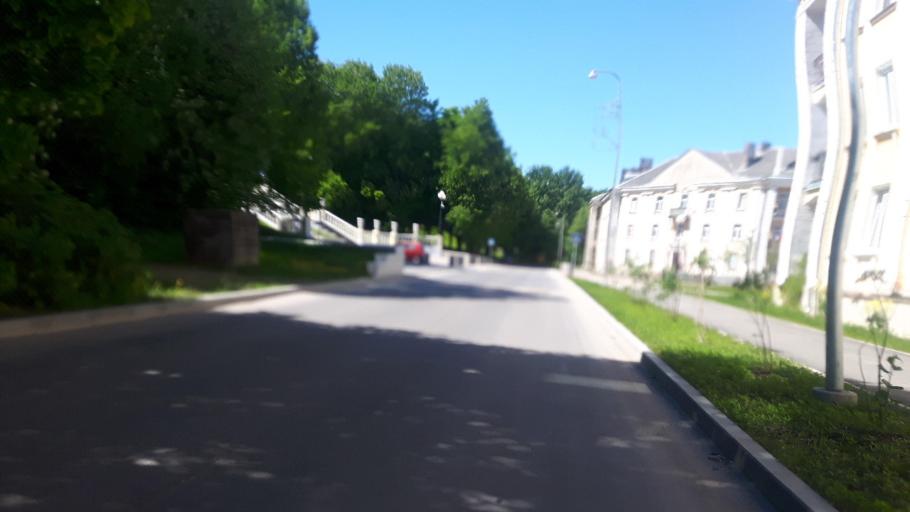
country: EE
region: Ida-Virumaa
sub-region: Sillamaee linn
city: Sillamae
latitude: 59.3968
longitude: 27.7645
